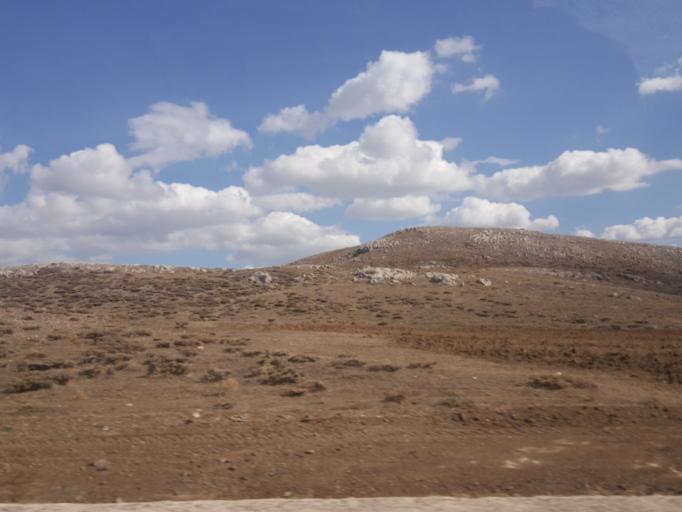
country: TR
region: Tokat
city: Artova
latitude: 40.1355
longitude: 36.3515
